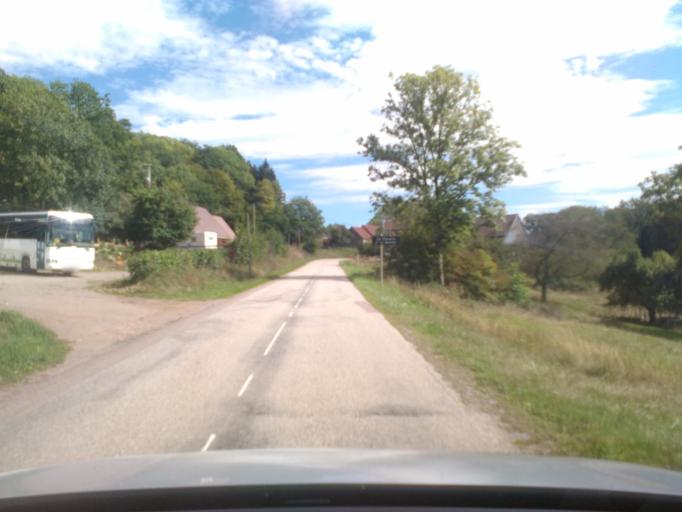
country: FR
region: Lorraine
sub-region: Departement des Vosges
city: Senones
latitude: 48.3809
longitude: 6.9630
